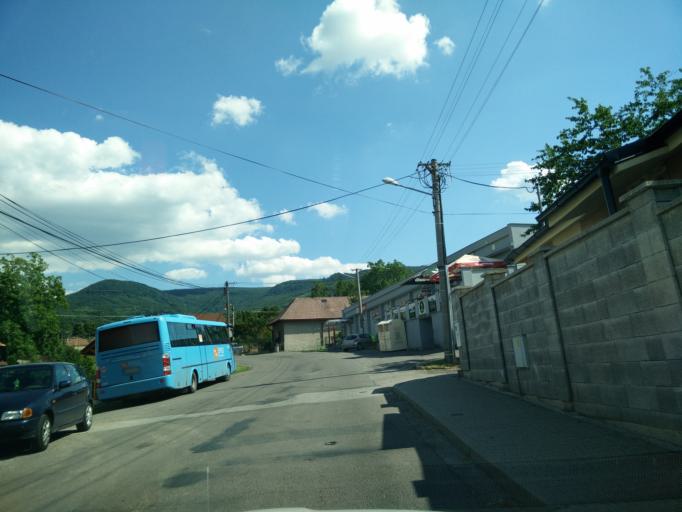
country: SK
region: Nitriansky
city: Prievidza
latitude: 48.7141
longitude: 18.6405
